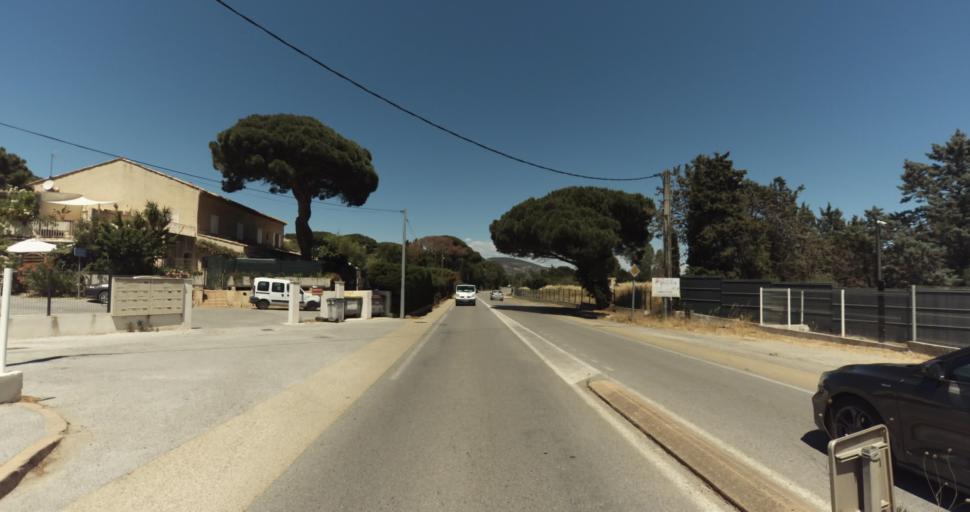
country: FR
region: Provence-Alpes-Cote d'Azur
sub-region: Departement du Var
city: Gassin
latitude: 43.2513
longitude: 6.5733
